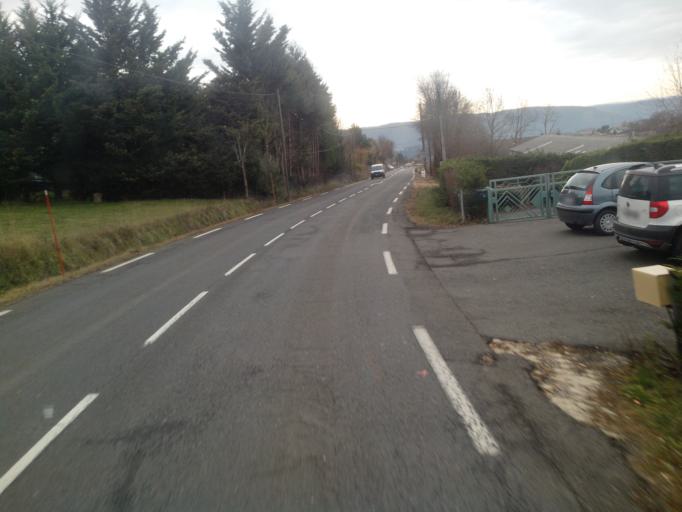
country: FR
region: Languedoc-Roussillon
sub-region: Departement de la Lozere
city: Mende
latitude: 44.5602
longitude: 3.5045
